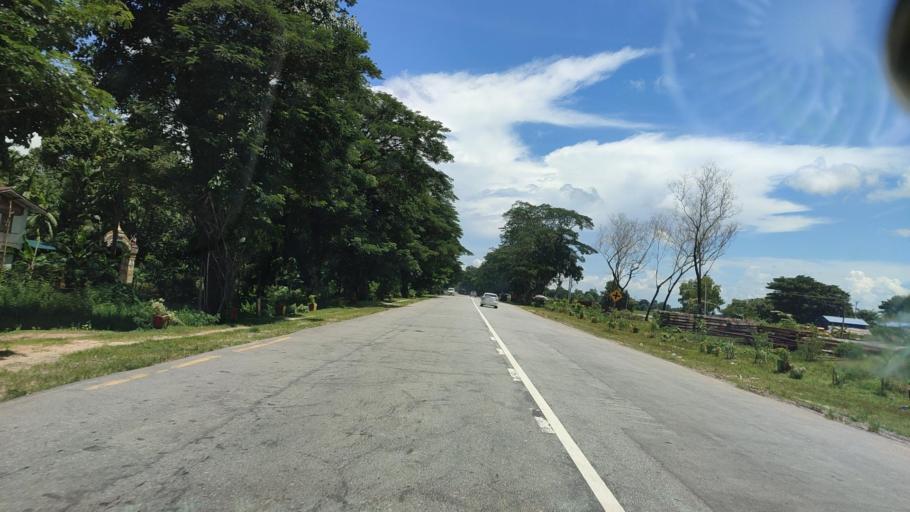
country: MM
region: Bago
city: Nyaunglebin
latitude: 18.1698
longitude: 96.6021
